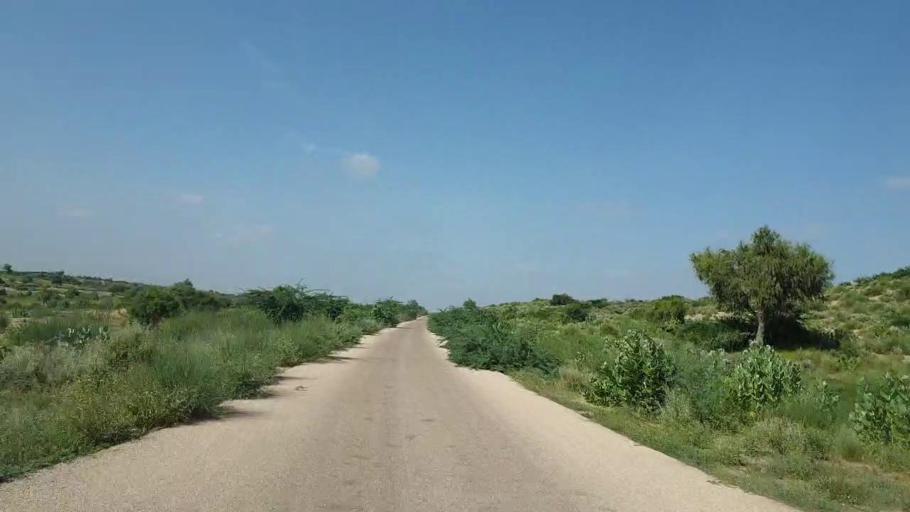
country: PK
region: Sindh
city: Mithi
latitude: 24.5366
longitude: 69.8593
